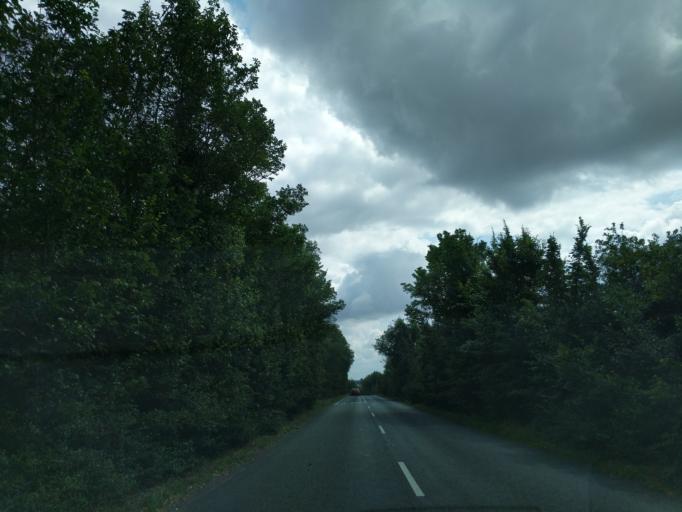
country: GB
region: England
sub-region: Cambridgeshire
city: Isleham
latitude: 52.3075
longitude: 0.4211
